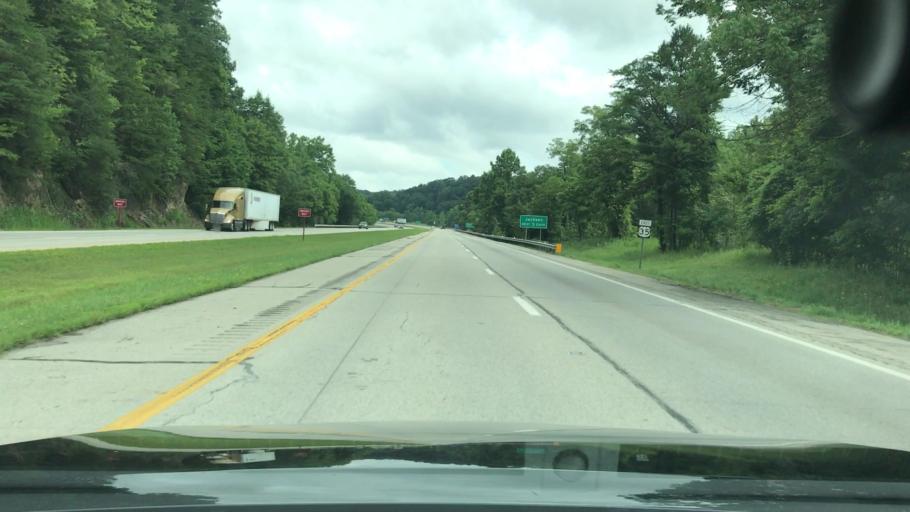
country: US
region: Ohio
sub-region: Jackson County
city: Jackson
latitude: 39.1031
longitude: -82.6716
